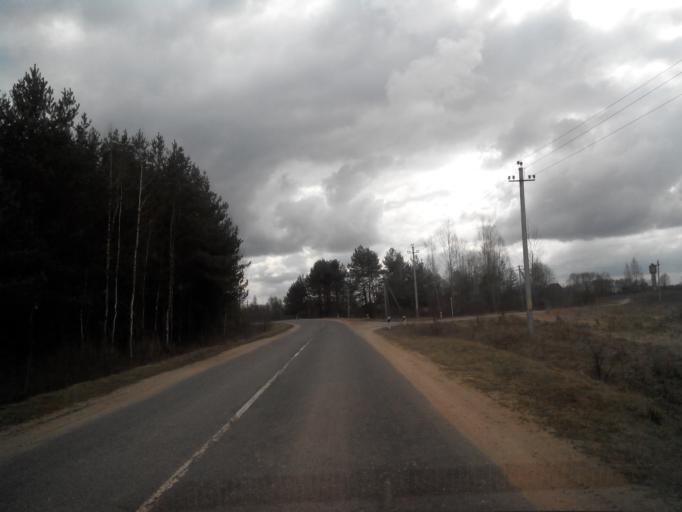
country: BY
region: Vitebsk
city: Pastavy
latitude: 55.0872
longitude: 26.8387
